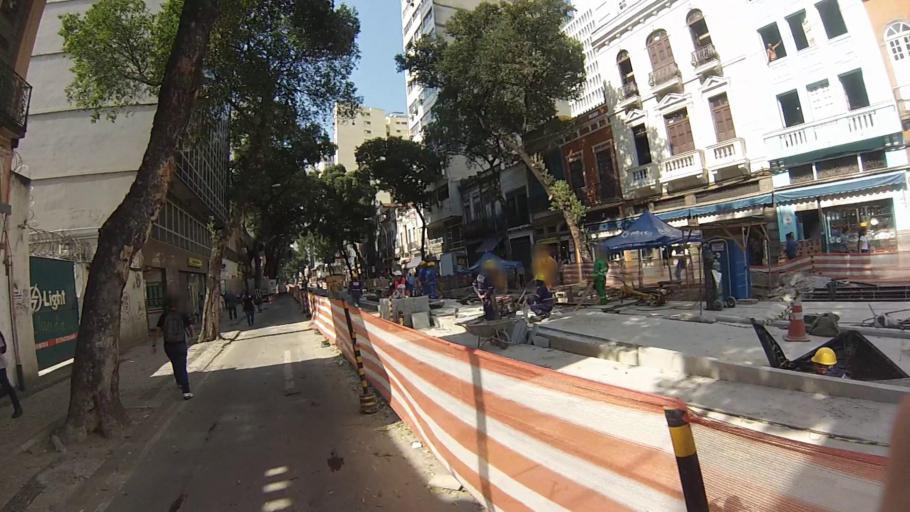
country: BR
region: Rio de Janeiro
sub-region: Rio De Janeiro
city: Rio de Janeiro
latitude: -22.9023
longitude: -43.1858
